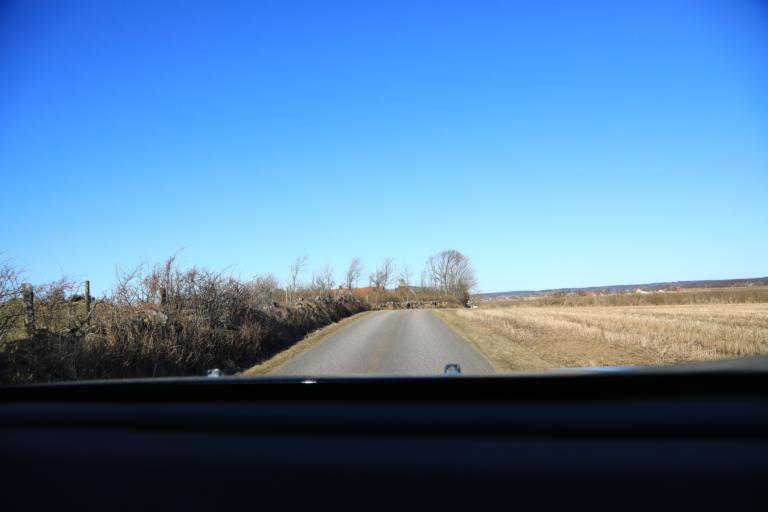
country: SE
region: Halland
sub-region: Kungsbacka Kommun
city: Frillesas
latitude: 57.2300
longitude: 12.1455
